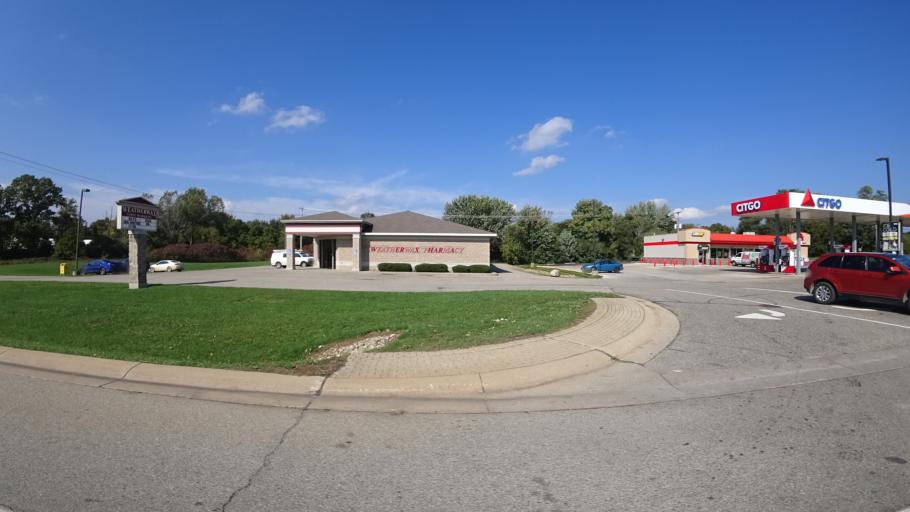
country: US
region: Michigan
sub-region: Jackson County
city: Spring Arbor
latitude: 42.2081
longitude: -84.5417
